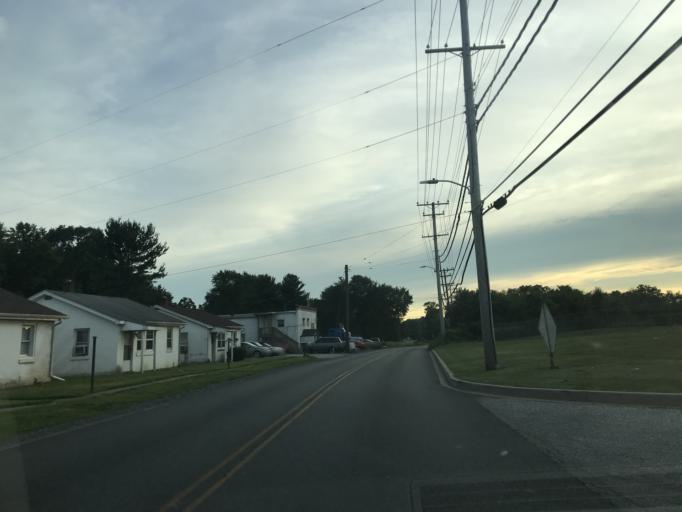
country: US
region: Maryland
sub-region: Harford County
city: Perryman
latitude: 39.4885
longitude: -76.1888
